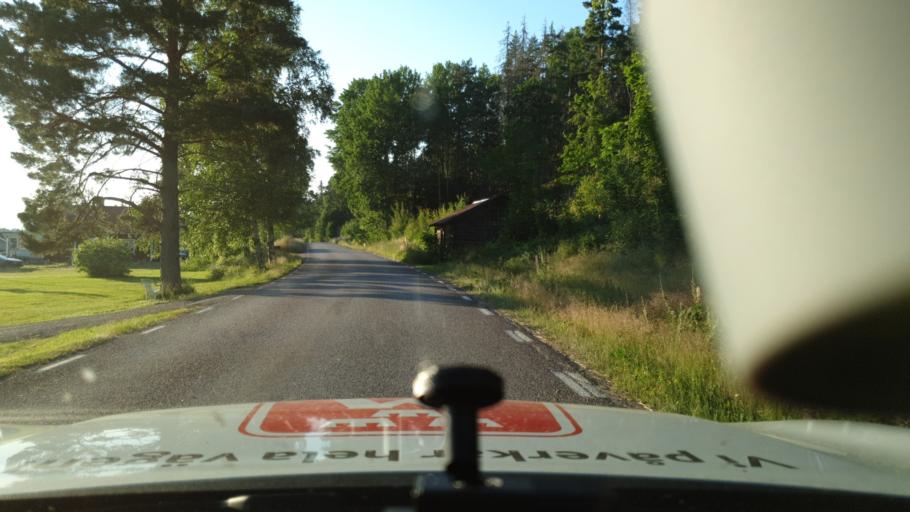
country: SE
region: Vaermland
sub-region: Kils Kommun
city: Kil
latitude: 59.6234
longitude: 13.3267
